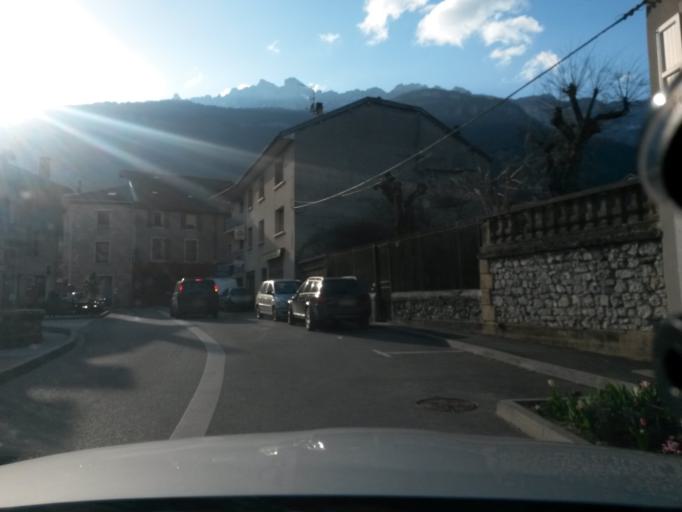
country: FR
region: Rhone-Alpes
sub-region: Departement de l'Isere
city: Le Touvet
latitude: 45.3583
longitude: 5.9525
